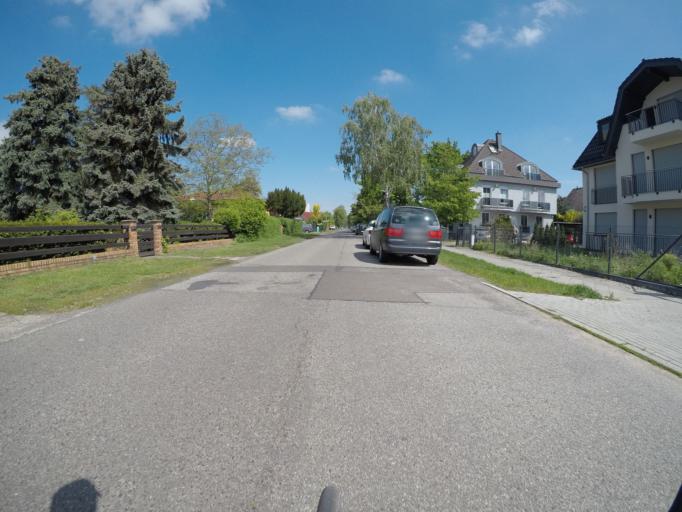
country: DE
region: Berlin
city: Biesdorf
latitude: 52.5275
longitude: 13.5504
